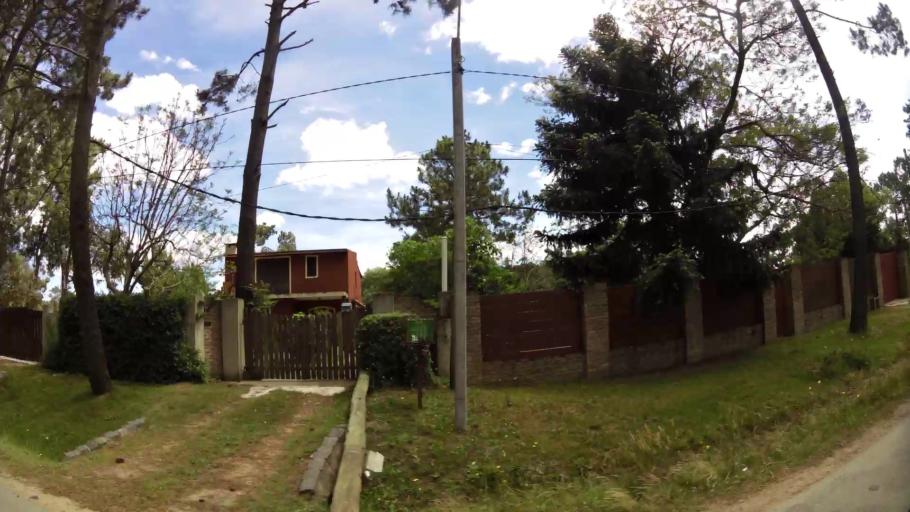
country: UY
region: Canelones
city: Empalme Olmos
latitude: -34.7891
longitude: -55.8898
